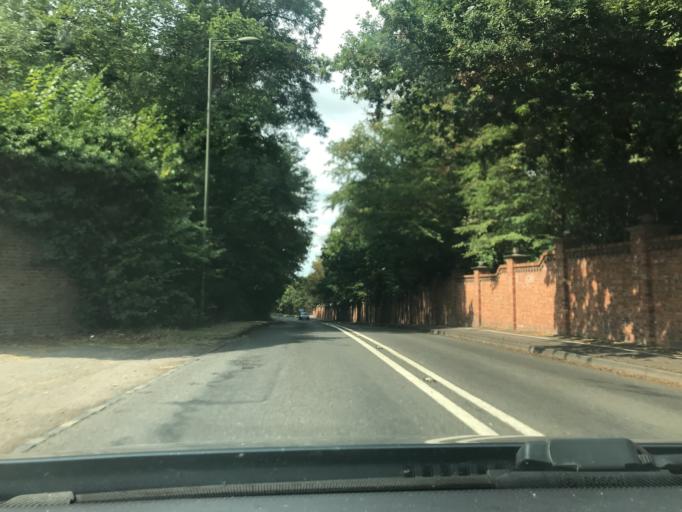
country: GB
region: England
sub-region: Surrey
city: Addlestone
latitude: 51.3791
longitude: -0.4858
